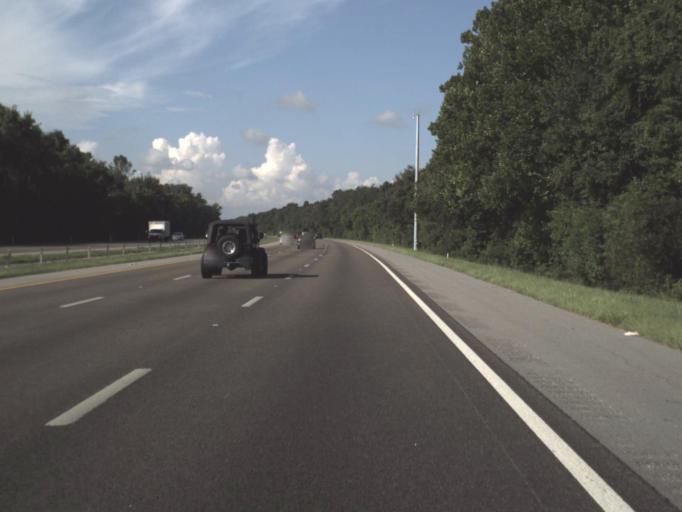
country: US
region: Florida
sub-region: Hillsborough County
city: Lutz
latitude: 28.1588
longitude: -82.4034
